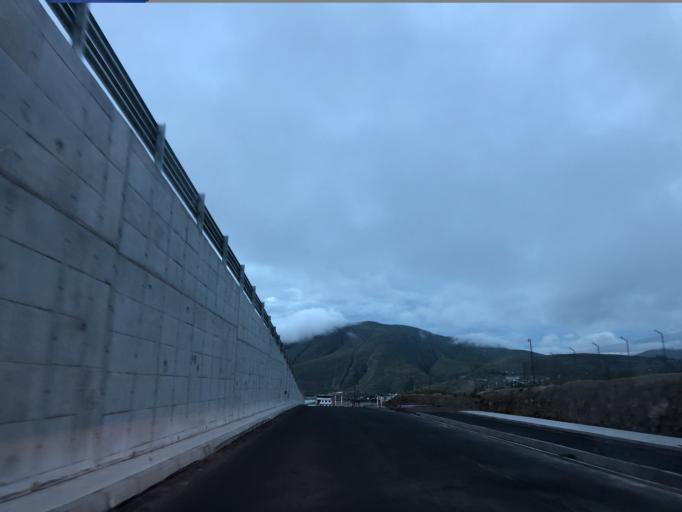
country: EC
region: Imbabura
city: Ibarra
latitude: 0.3740
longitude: -78.1277
